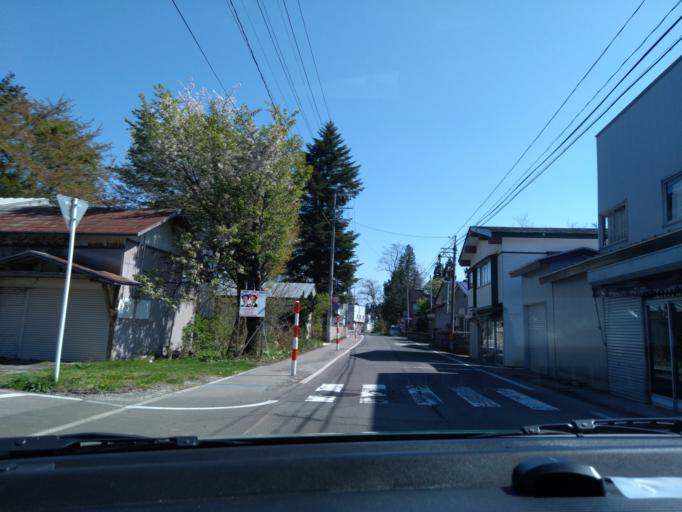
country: JP
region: Akita
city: Kakunodatemachi
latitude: 39.5572
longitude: 140.5856
